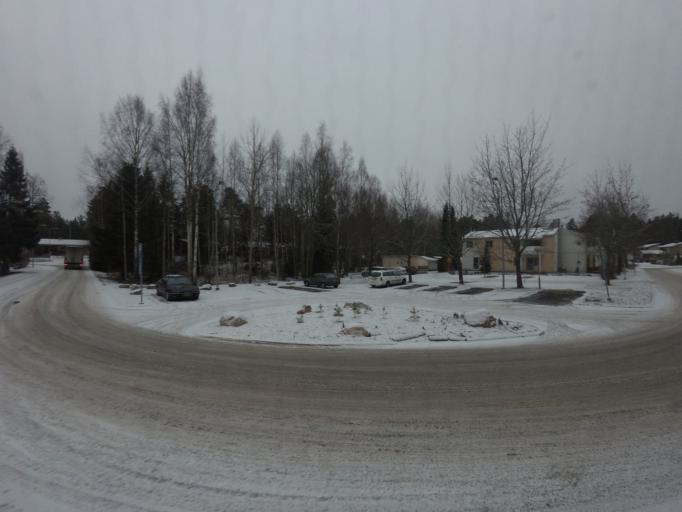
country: FI
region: Uusimaa
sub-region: Helsinki
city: Espoo
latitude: 60.2042
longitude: 24.6281
